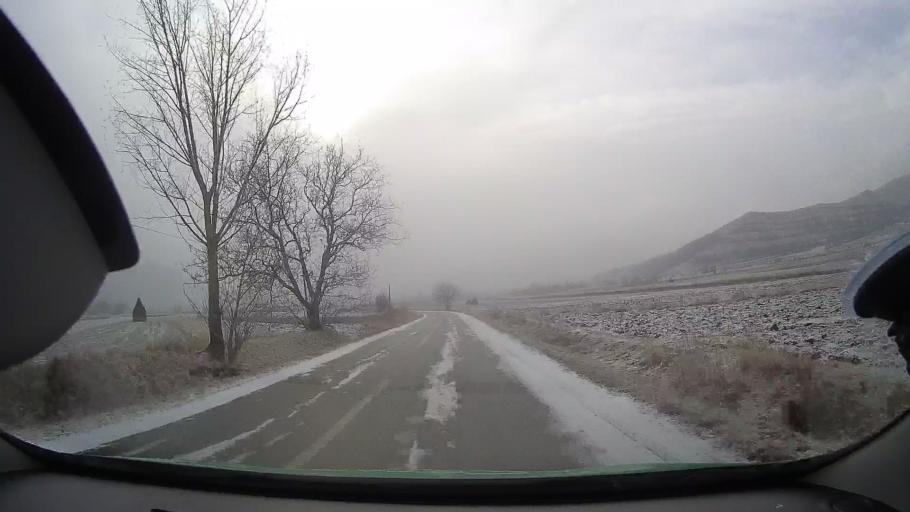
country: RO
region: Alba
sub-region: Comuna Rimetea
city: Rimetea
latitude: 46.4150
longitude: 23.5580
